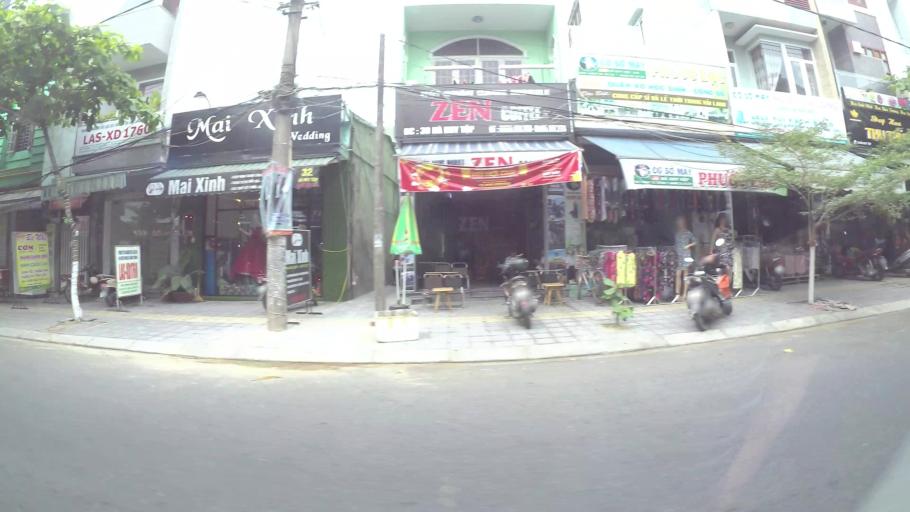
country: VN
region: Da Nang
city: Thanh Khe
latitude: 16.0703
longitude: 108.1917
